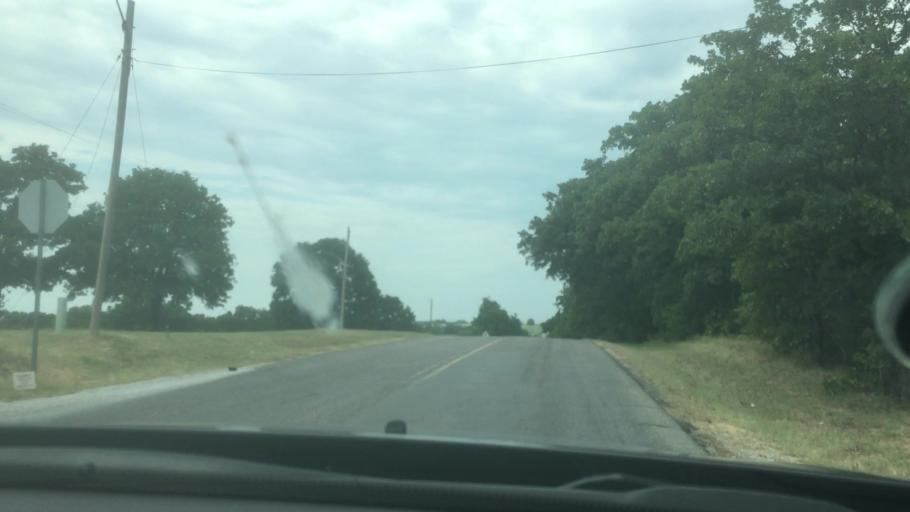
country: US
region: Oklahoma
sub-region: Murray County
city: Davis
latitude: 34.4917
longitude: -97.0555
